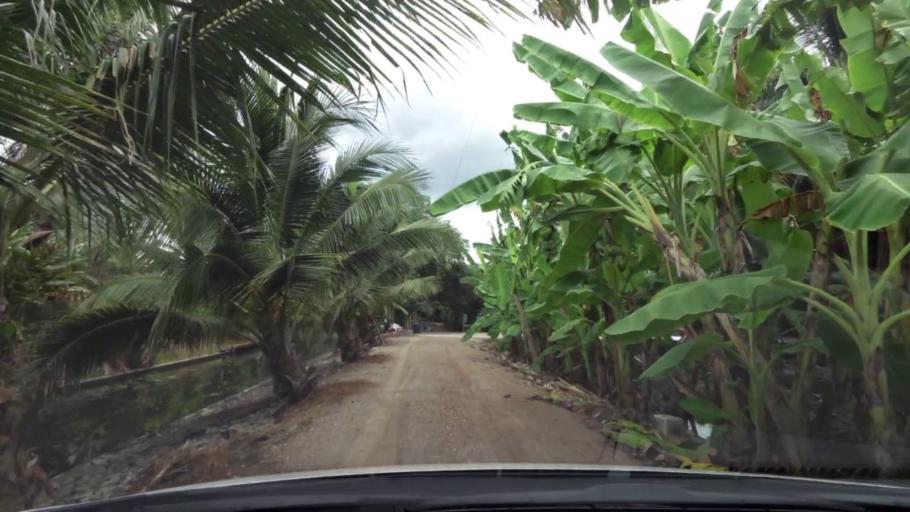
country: TH
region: Ratchaburi
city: Damnoen Saduak
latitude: 13.5497
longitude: 99.9928
